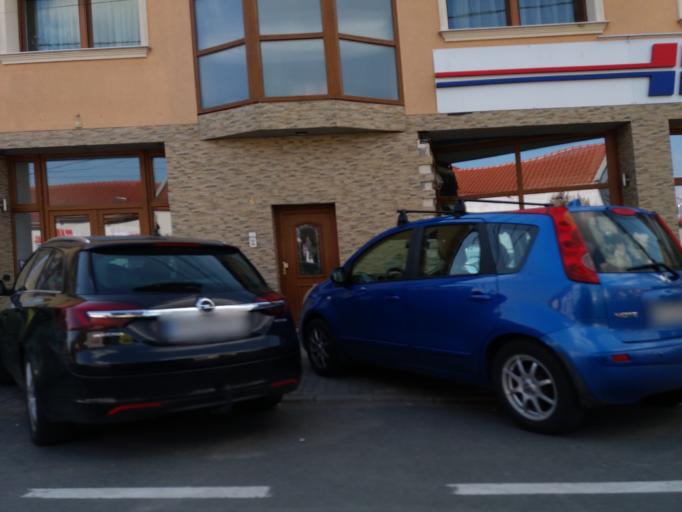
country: RO
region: Arad
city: Arad
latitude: 46.1786
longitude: 21.3081
